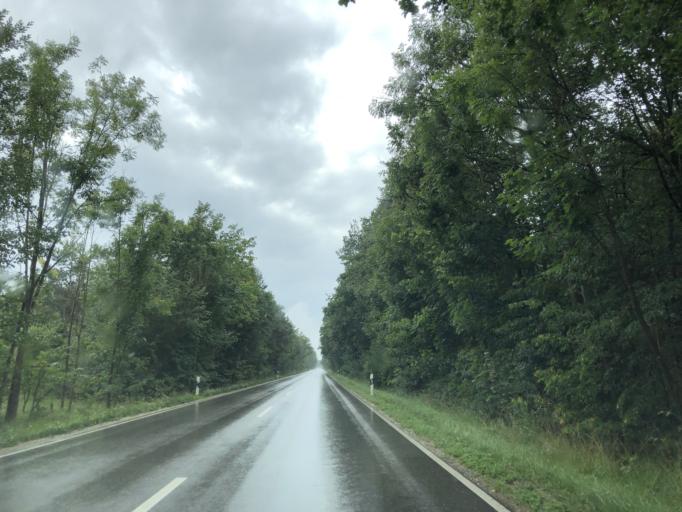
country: DE
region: Bavaria
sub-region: Upper Bavaria
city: Eching
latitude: 48.2771
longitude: 11.6051
